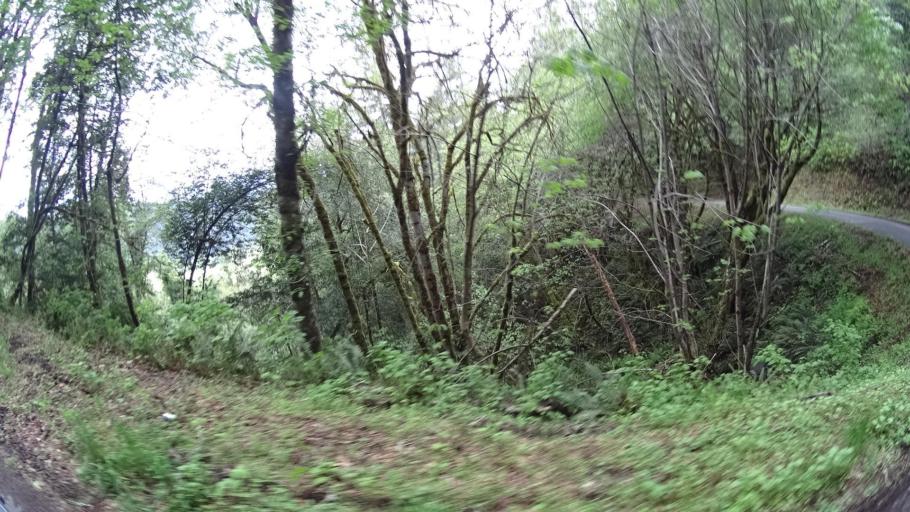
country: US
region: California
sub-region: Humboldt County
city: Blue Lake
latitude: 40.7593
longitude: -123.9064
